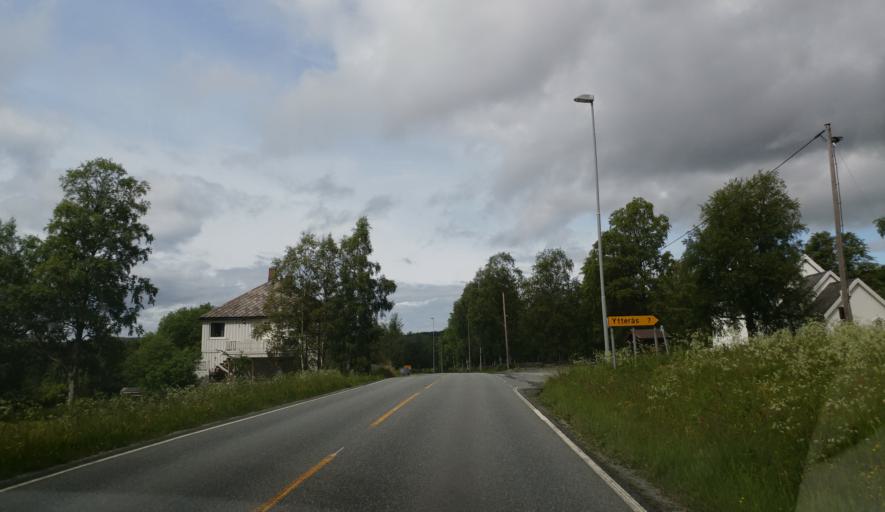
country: NO
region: Nord-Trondelag
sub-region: Stjordal
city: Stjordalshalsen
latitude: 63.3929
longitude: 11.0668
